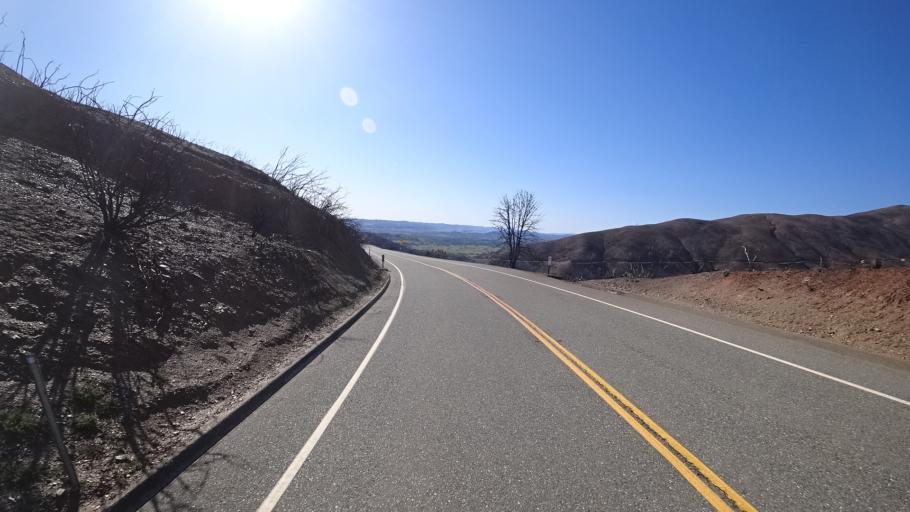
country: US
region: California
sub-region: Tehama County
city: Rancho Tehama Reserve
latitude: 39.6489
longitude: -122.6154
